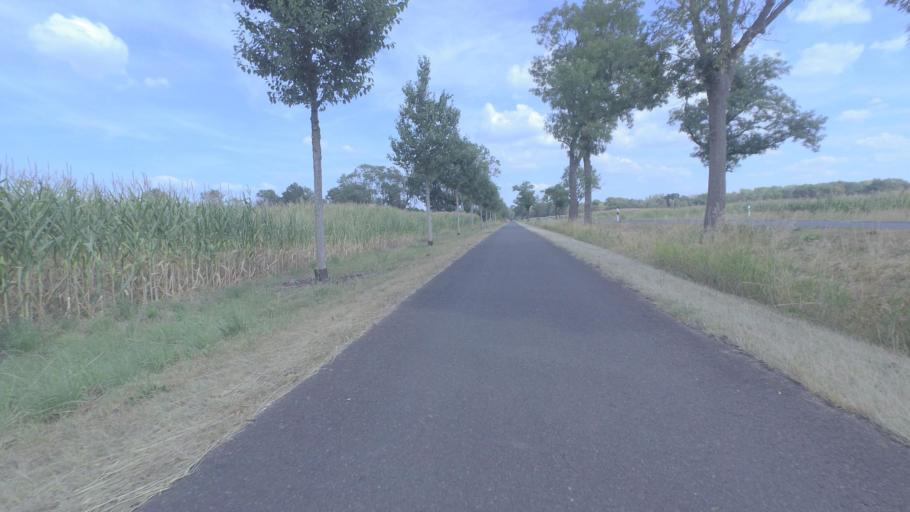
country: DE
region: Brandenburg
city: Nauen
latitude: 52.6375
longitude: 12.9130
